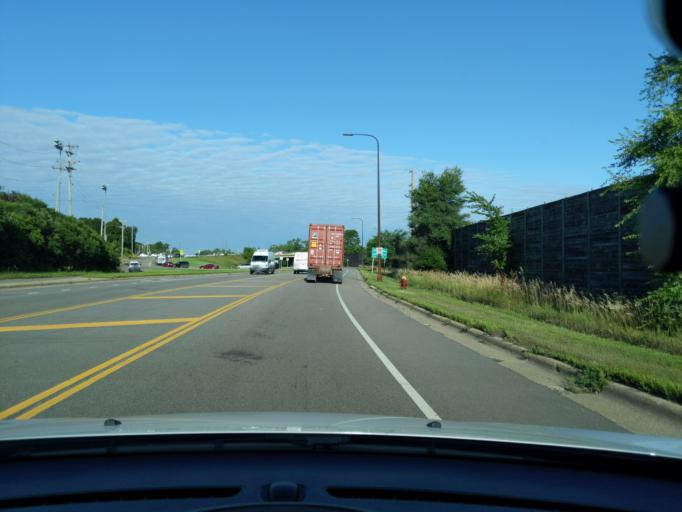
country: US
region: Minnesota
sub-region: Ramsey County
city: Falcon Heights
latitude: 44.9690
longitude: -93.1634
